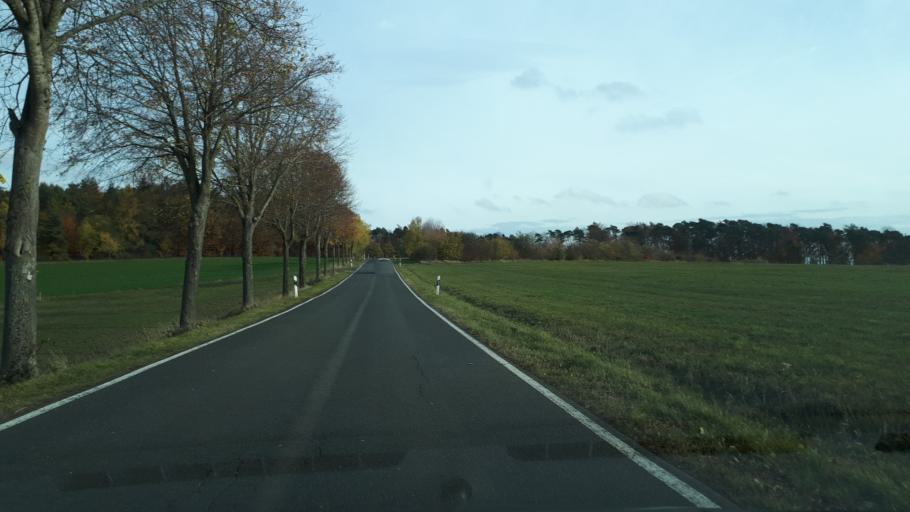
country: DE
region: Rheinland-Pfalz
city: Gillenbeuren
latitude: 50.1521
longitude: 7.0220
